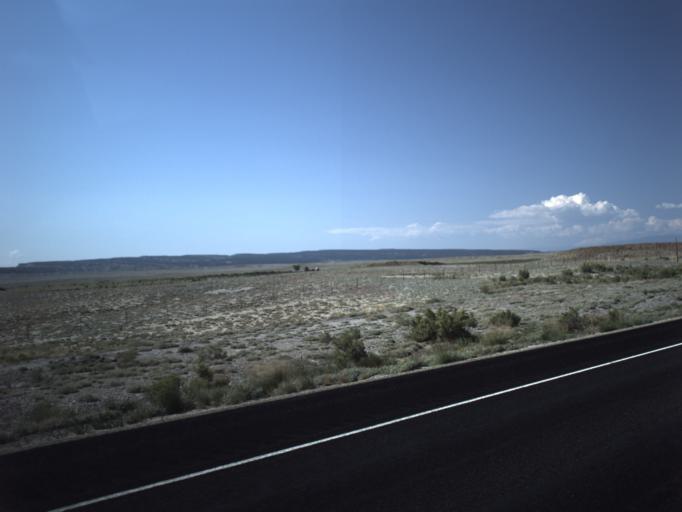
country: US
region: Utah
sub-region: Emery County
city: Ferron
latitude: 39.0246
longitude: -111.1350
